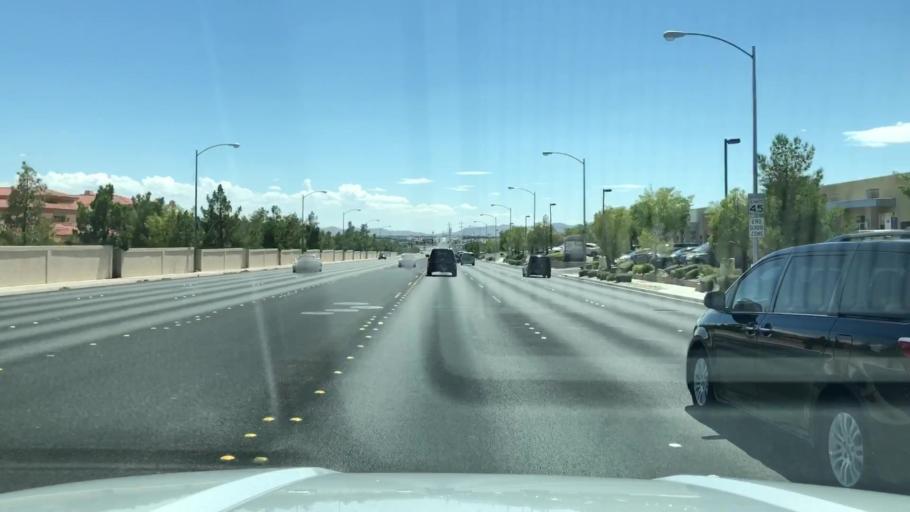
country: US
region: Nevada
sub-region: Clark County
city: Spring Valley
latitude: 36.0960
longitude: -115.2792
